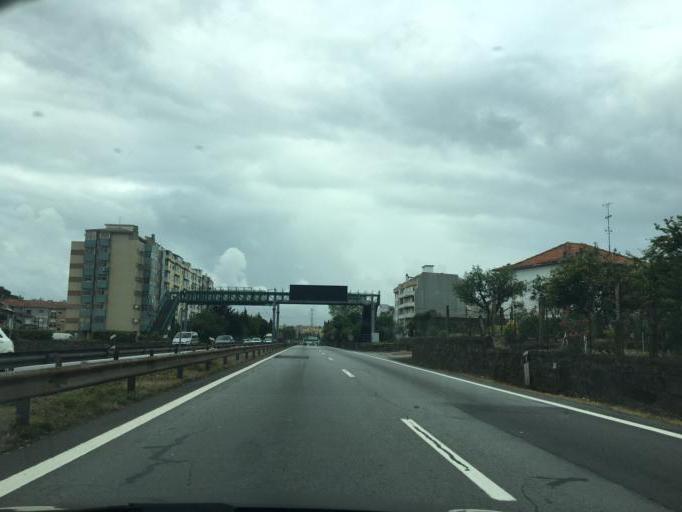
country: PT
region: Porto
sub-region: Matosinhos
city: Senhora da Hora
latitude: 41.1891
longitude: -8.6267
